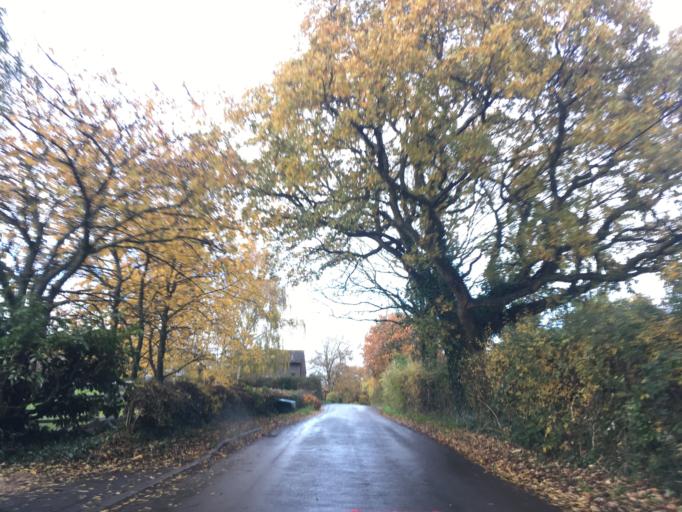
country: GB
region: England
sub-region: South Gloucestershire
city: Winterbourne
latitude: 51.5150
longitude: -2.4650
